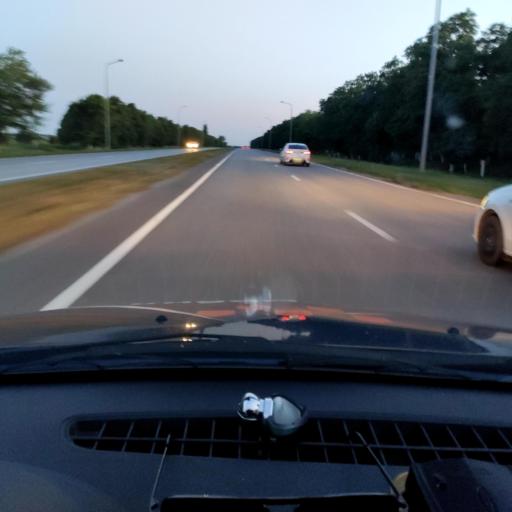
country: RU
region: Belgorod
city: Bekhteyevka
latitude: 50.8529
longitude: 37.1729
